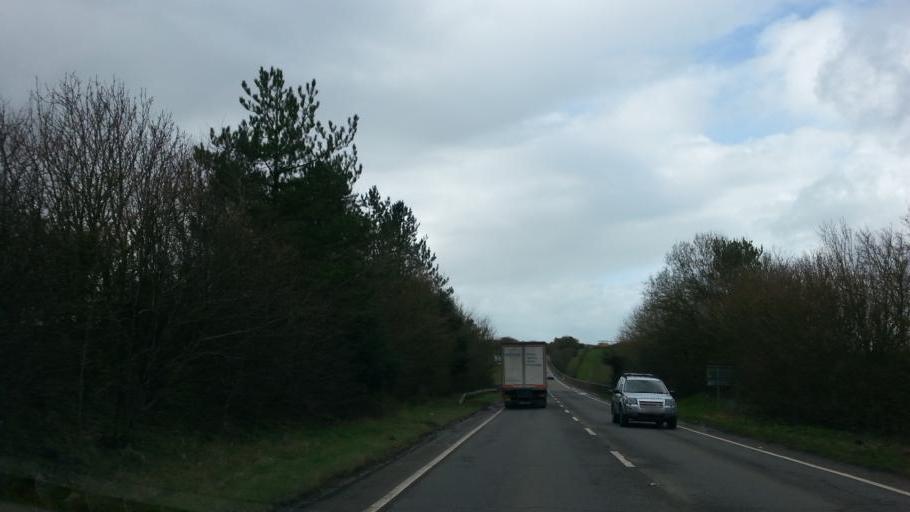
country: GB
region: England
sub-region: Devon
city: Northam
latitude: 51.0247
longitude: -4.2322
